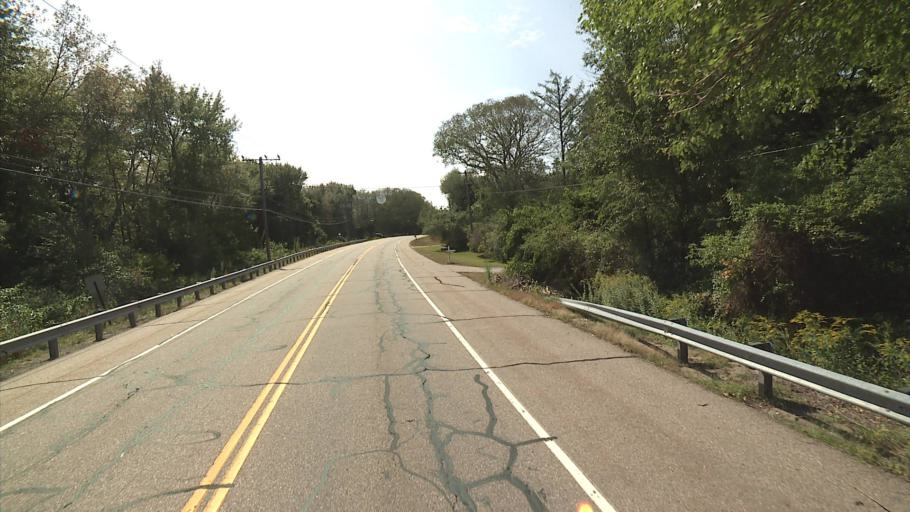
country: US
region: Connecticut
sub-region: New London County
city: Lisbon
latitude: 41.5942
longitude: -72.0193
